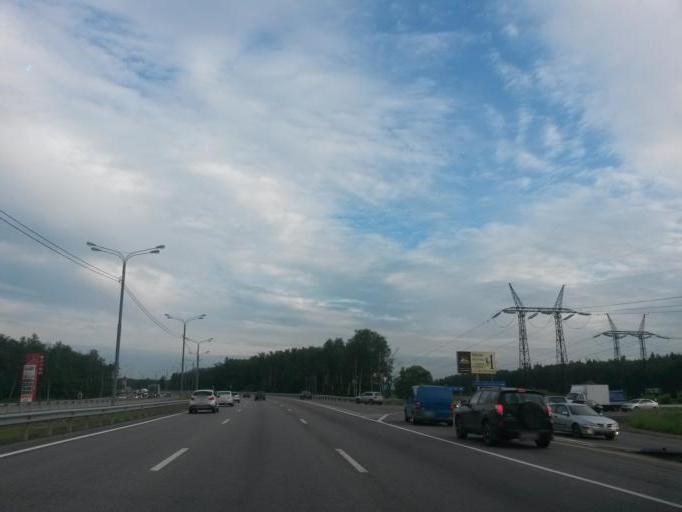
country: RU
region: Moskovskaya
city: Vostryakovo
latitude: 55.3690
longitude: 37.7824
